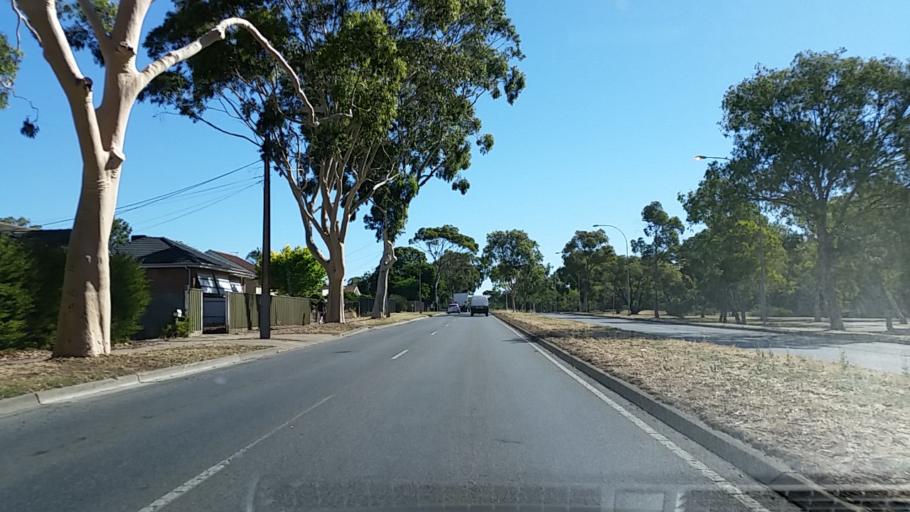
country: AU
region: South Australia
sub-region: Salisbury
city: Ingle Farm
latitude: -34.8123
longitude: 138.6443
